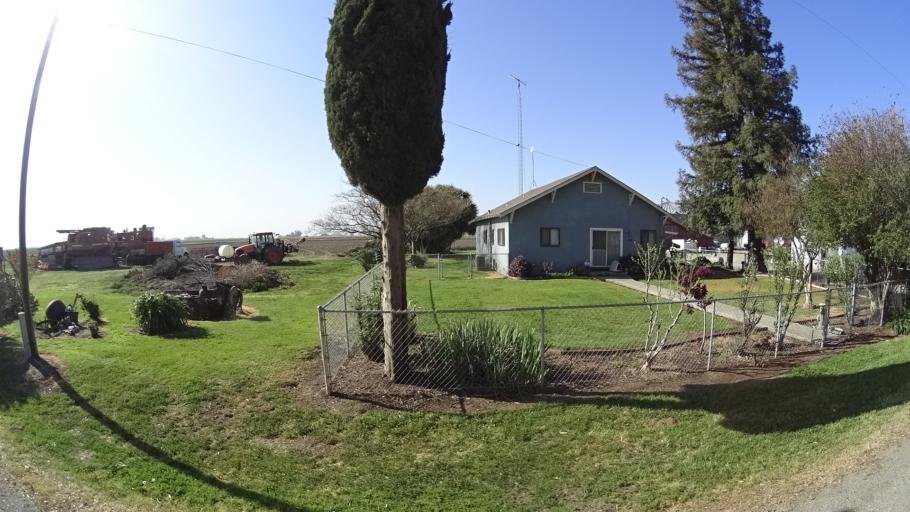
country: US
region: California
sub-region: Glenn County
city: Willows
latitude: 39.5726
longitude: -122.0969
